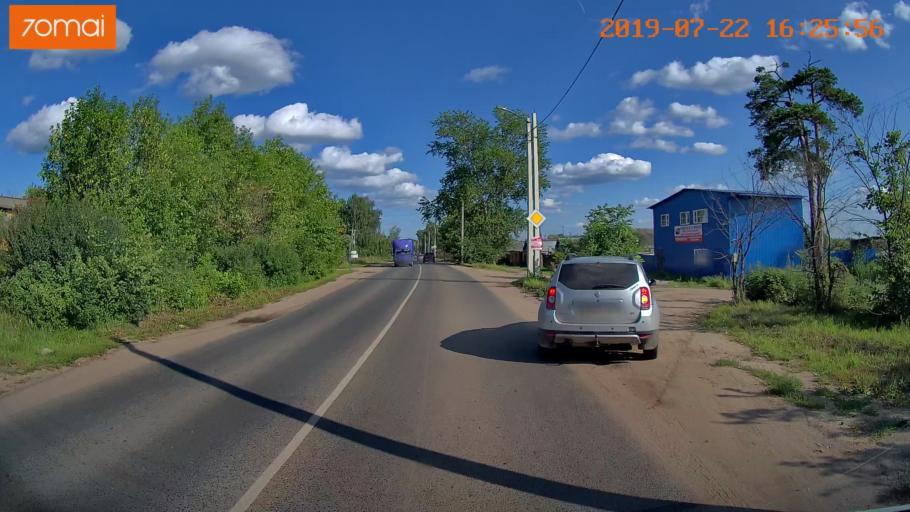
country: RU
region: Ivanovo
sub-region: Gorod Ivanovo
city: Ivanovo
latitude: 57.0513
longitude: 40.9286
